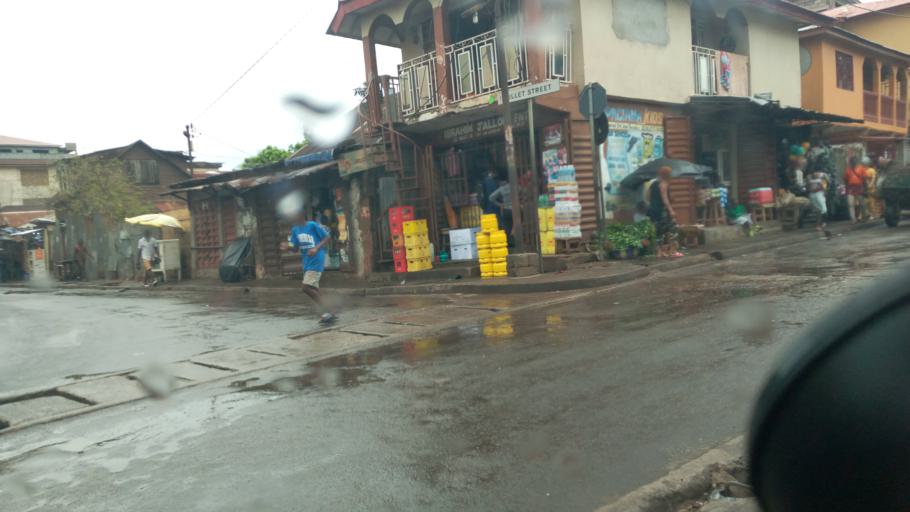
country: SL
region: Western Area
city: Freetown
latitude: 8.4759
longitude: -13.2392
